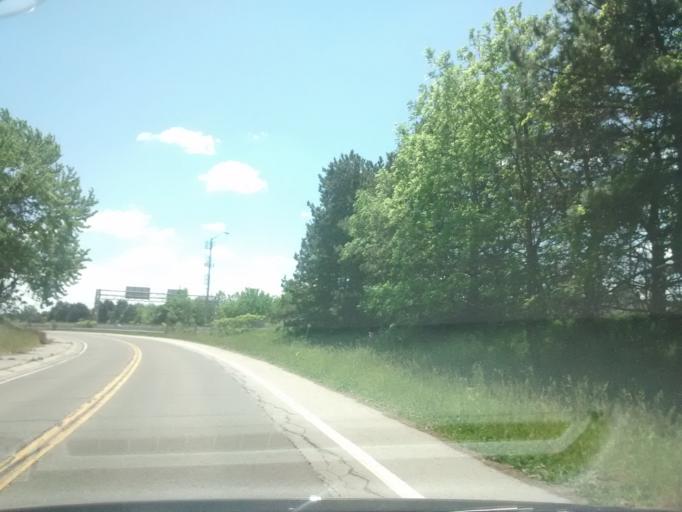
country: CA
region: Ontario
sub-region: Regional Municipality of Niagara
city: St. Catharines
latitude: 43.1803
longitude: -79.3581
